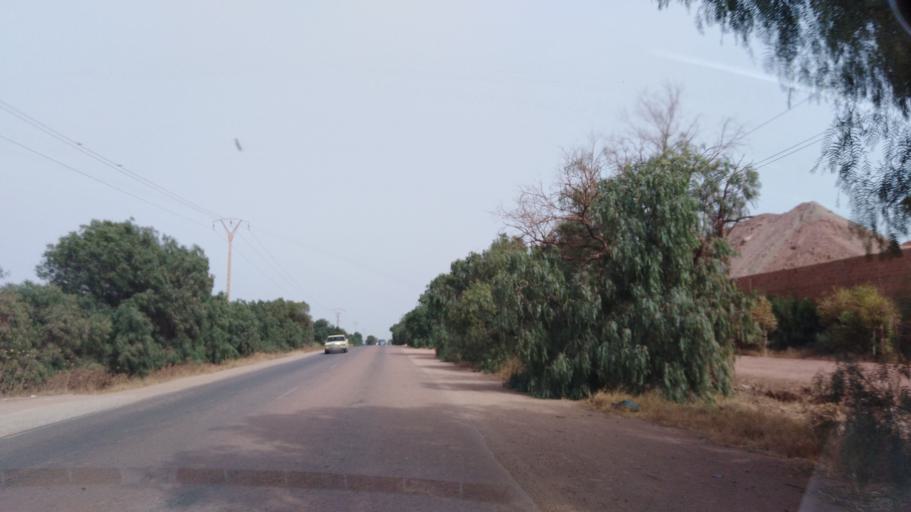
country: MA
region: Chaouia-Ouardigha
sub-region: Settat Province
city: Berrechid
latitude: 33.2435
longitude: -7.5497
